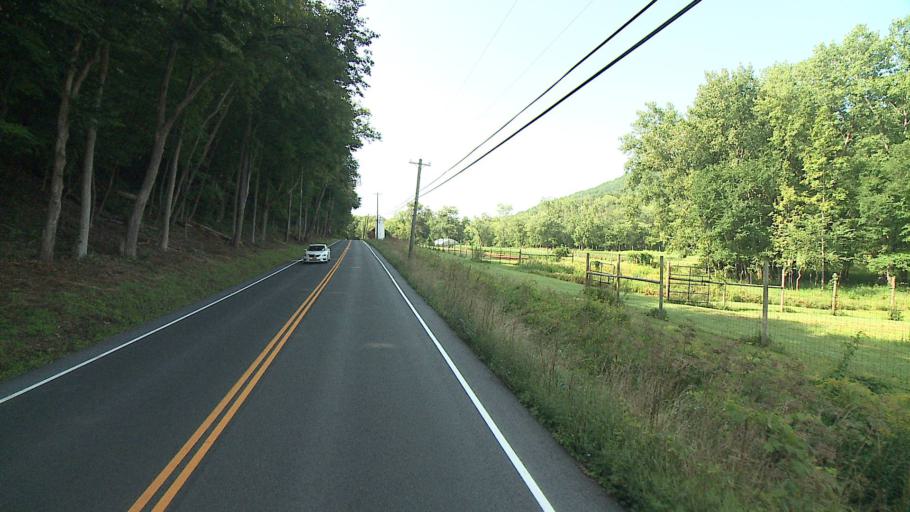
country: US
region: Connecticut
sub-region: Litchfield County
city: Kent
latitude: 41.6970
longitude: -73.4957
